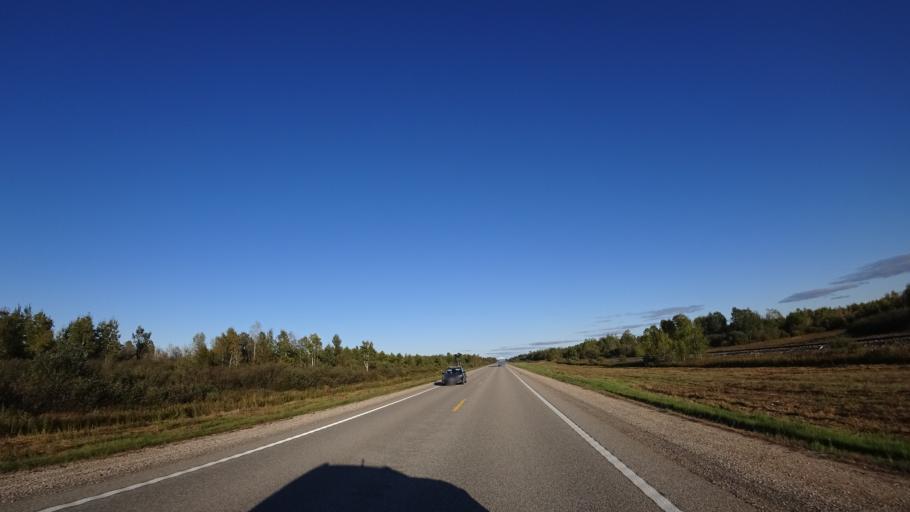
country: US
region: Michigan
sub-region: Schoolcraft County
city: Manistique
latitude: 46.3455
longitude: -86.1396
